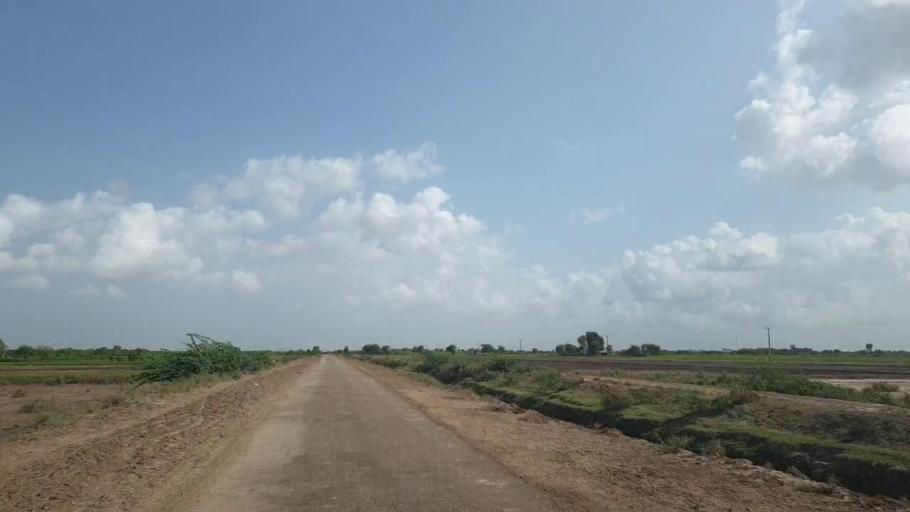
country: PK
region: Sindh
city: Kadhan
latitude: 24.5682
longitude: 69.0675
